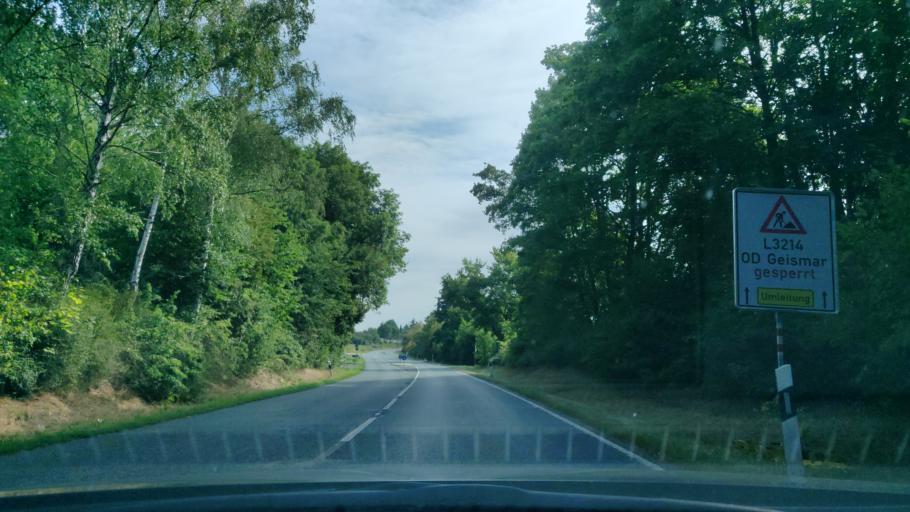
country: DE
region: Hesse
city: Fritzlar
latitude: 51.1368
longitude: 9.2558
